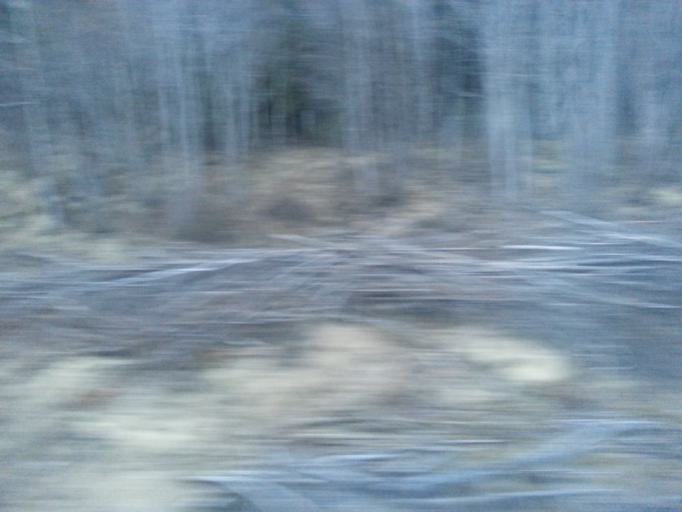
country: NO
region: Sor-Trondelag
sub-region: Rennebu
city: Berkak
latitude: 62.7697
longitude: 9.9897
